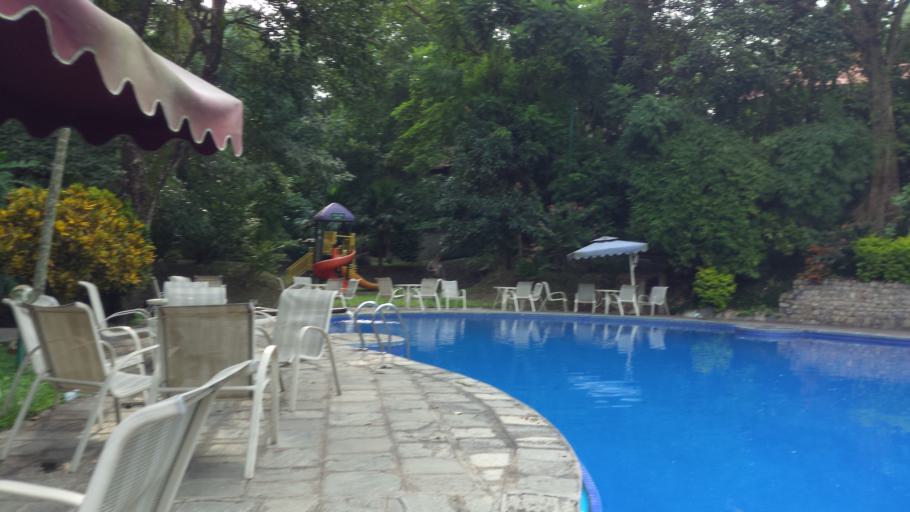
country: NP
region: Central Region
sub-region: Narayani Zone
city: Bharatpur
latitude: 27.8750
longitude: 84.6160
